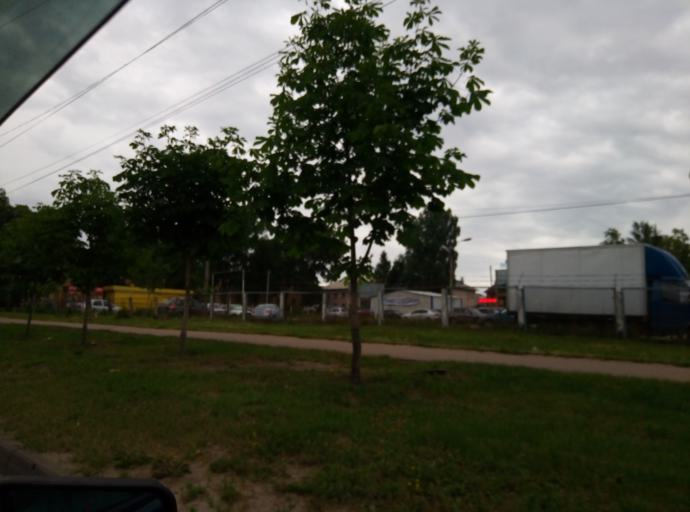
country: RU
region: Kursk
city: Kursk
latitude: 51.7096
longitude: 36.1484
